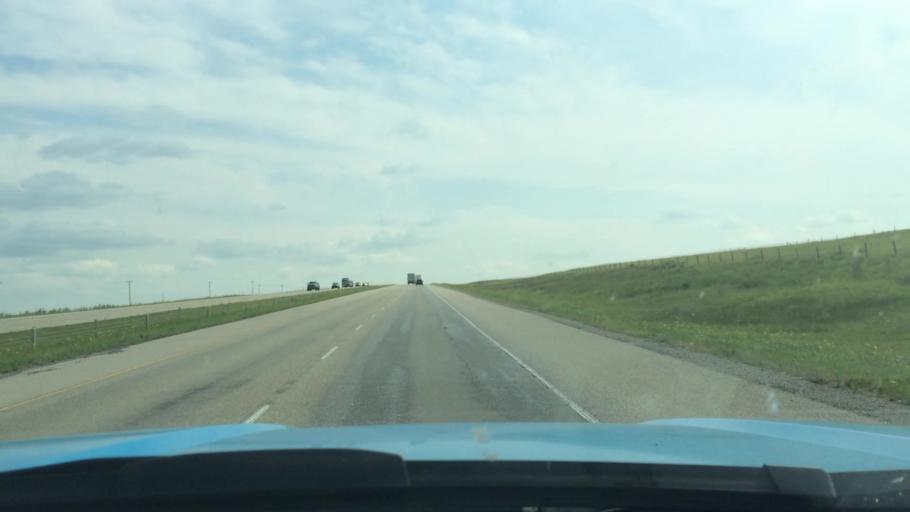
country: CA
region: Alberta
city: Carstairs
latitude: 51.5463
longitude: -114.0254
